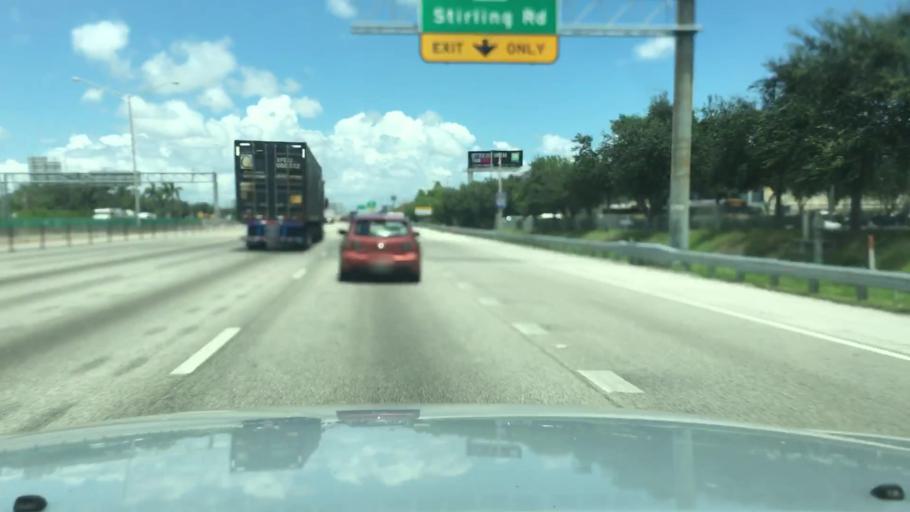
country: US
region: Florida
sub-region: Broward County
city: Dania Beach
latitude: 26.0388
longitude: -80.1632
